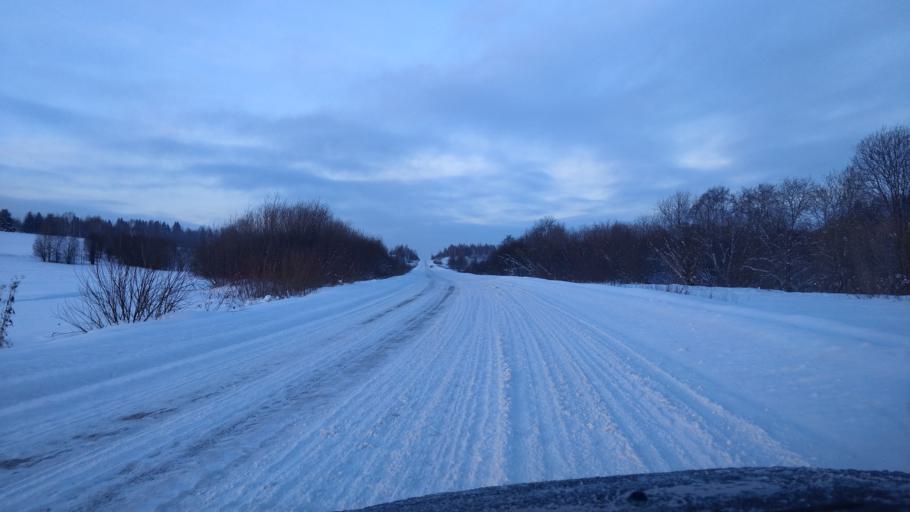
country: RU
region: Perm
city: Verkhnechusovskiye Gorodki
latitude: 58.2025
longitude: 57.1446
